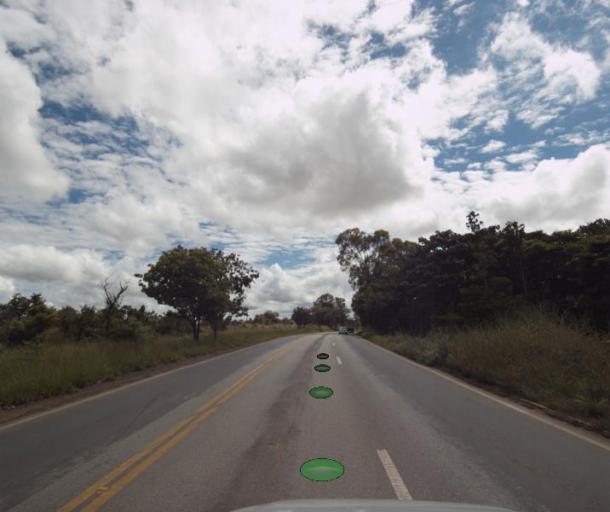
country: BR
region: Goias
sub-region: Uruacu
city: Uruacu
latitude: -14.3532
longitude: -49.1586
